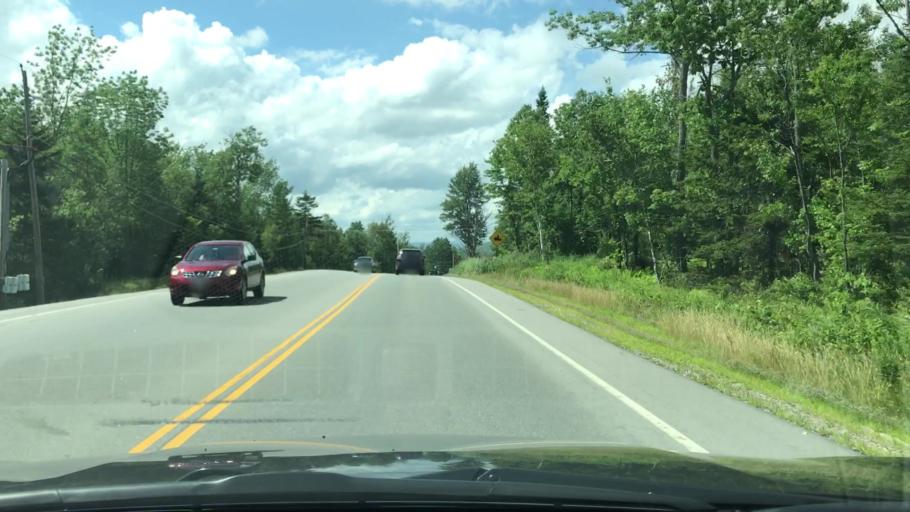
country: US
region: New Hampshire
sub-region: Coos County
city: Jefferson
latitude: 44.3738
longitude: -71.4093
